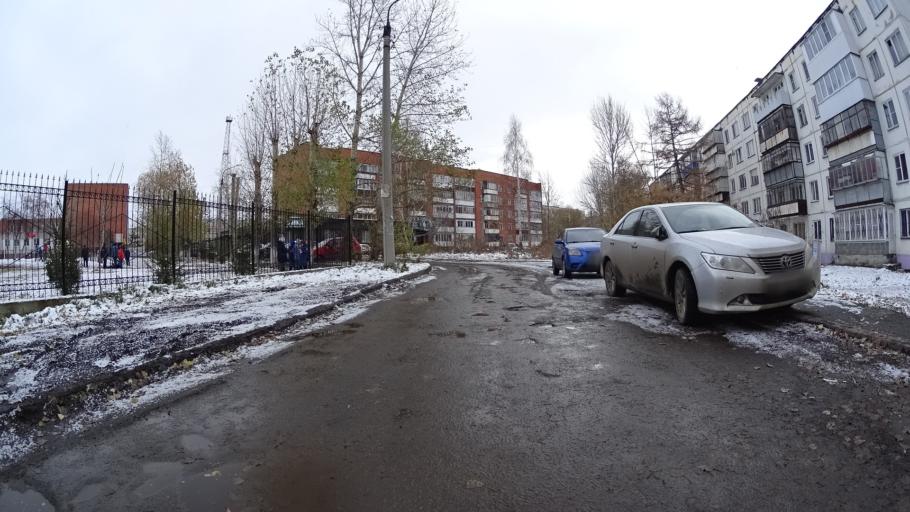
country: RU
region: Chelyabinsk
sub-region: Gorod Chelyabinsk
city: Chelyabinsk
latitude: 55.1913
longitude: 61.3080
